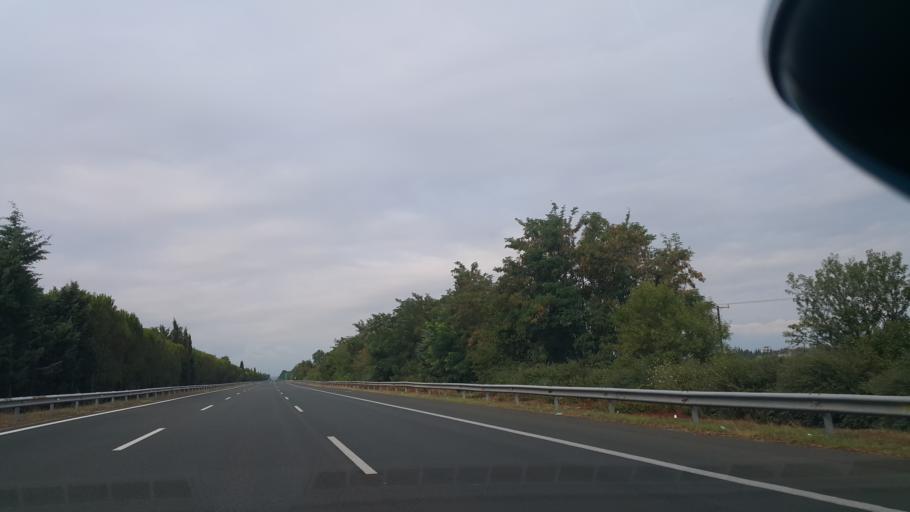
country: GR
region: Central Macedonia
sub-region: Nomos Pierias
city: Korinos
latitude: 40.3100
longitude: 22.5613
